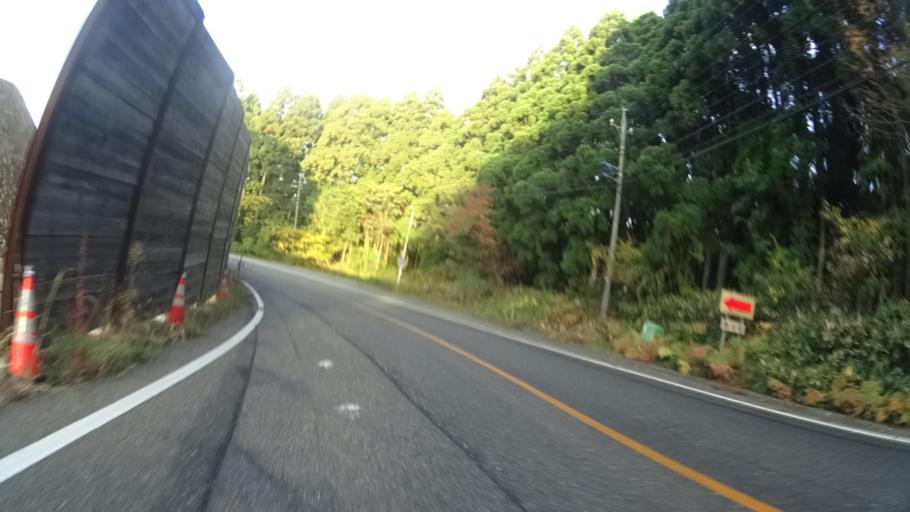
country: JP
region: Ishikawa
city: Nanao
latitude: 37.1763
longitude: 136.7148
